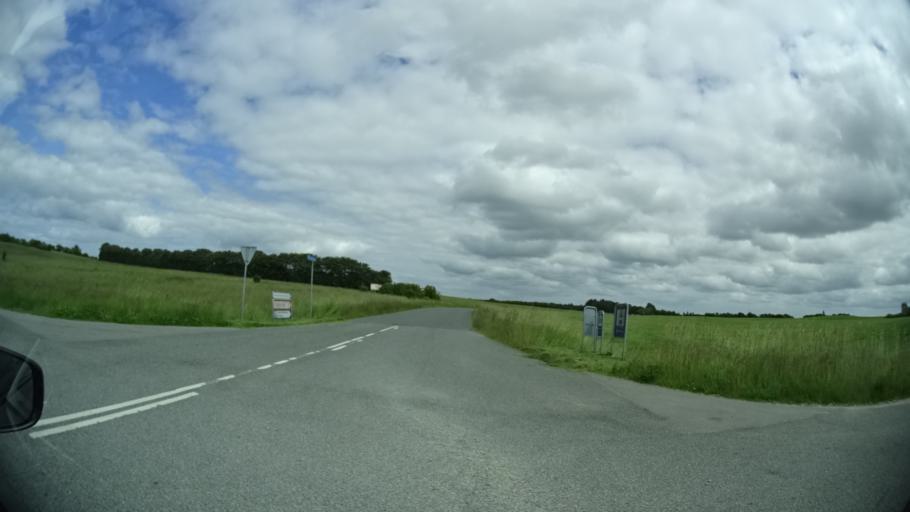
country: DK
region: Central Jutland
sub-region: Norddjurs Kommune
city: Grenaa
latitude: 56.5195
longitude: 10.7248
